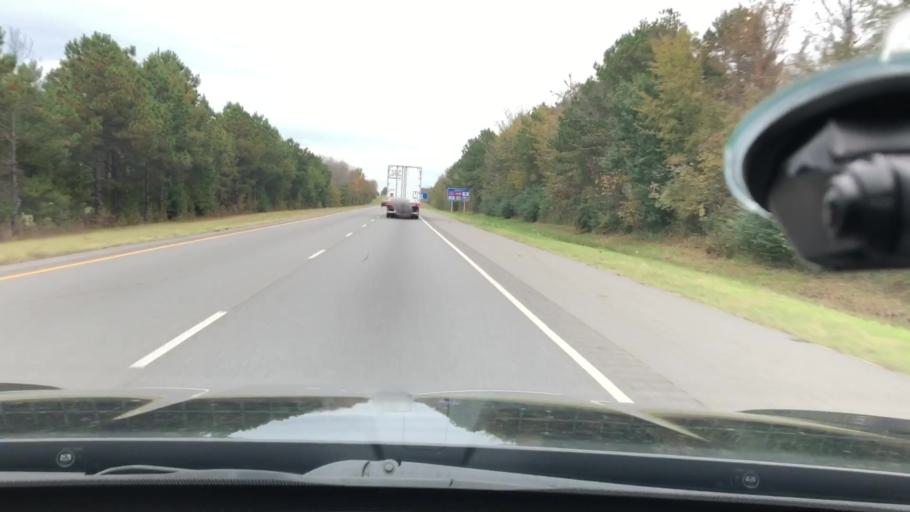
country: US
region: Arkansas
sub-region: Hempstead County
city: Hope
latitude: 33.6702
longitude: -93.6264
